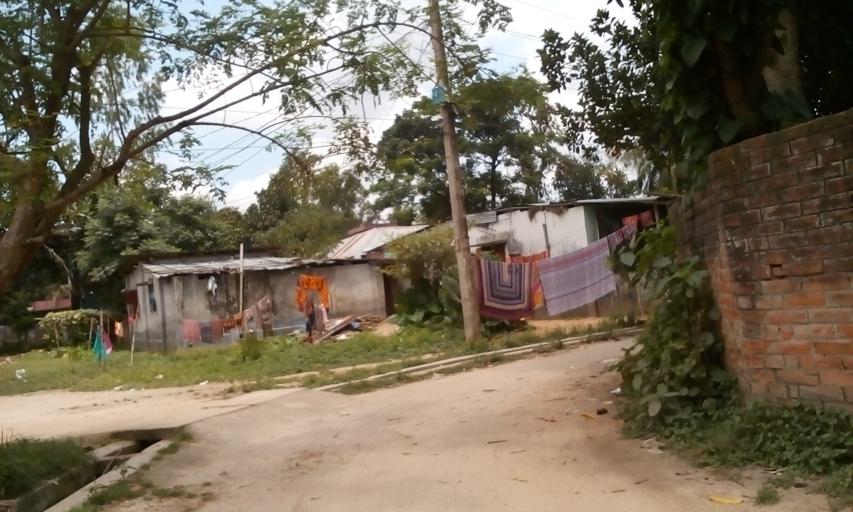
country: IN
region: West Bengal
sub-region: Dakshin Dinajpur
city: Balurghat
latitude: 25.3859
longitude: 88.9953
